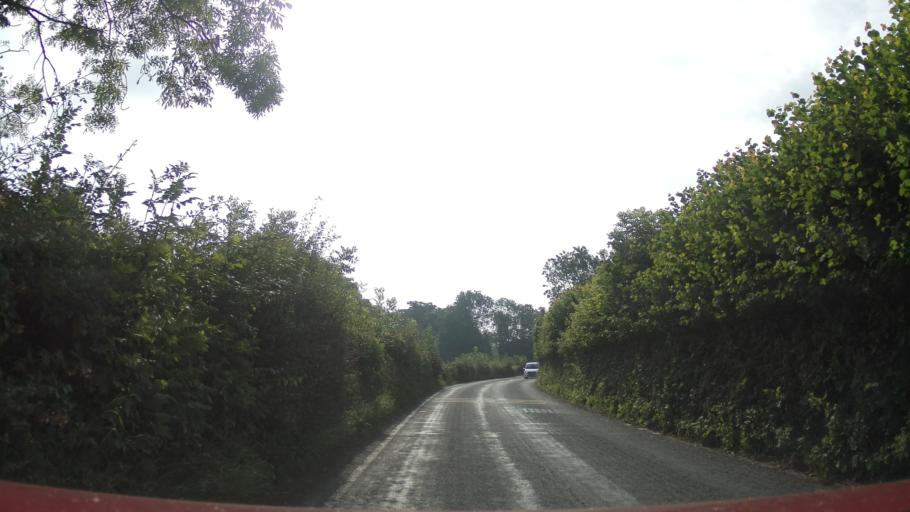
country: GB
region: England
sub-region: Bath and North East Somerset
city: East Harptree
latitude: 51.2797
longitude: -2.5847
